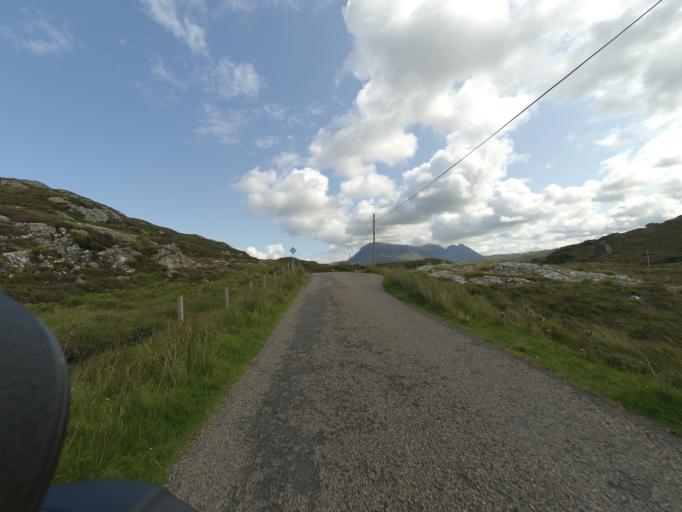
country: GB
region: Scotland
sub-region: Highland
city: Ullapool
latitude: 58.2417
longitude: -5.1823
